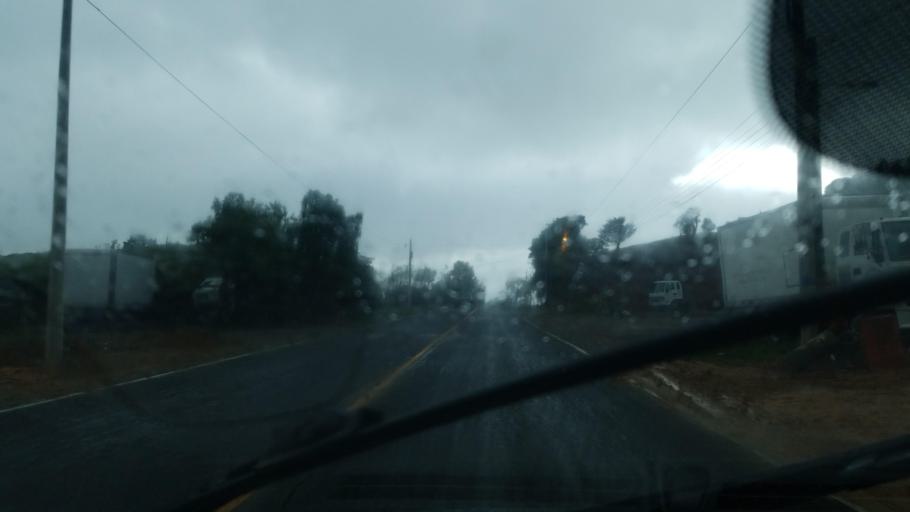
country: HN
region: Ocotepeque
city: La Labor
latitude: 14.4683
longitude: -89.0881
